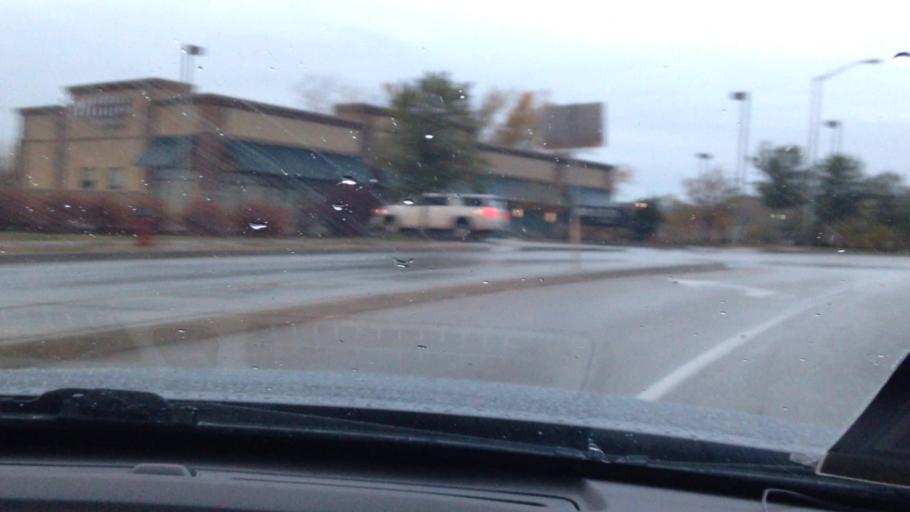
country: US
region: Missouri
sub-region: Platte County
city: Parkville
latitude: 39.2112
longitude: -94.6432
